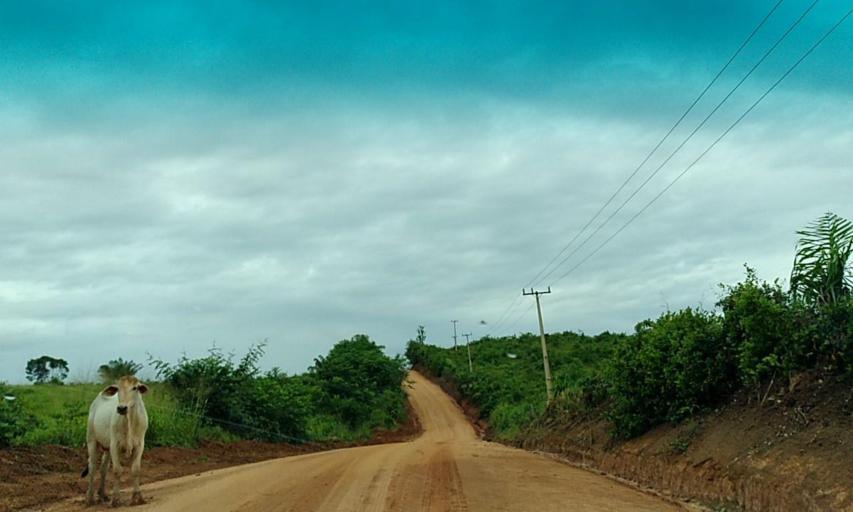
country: BR
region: Para
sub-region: Altamira
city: Altamira
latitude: -3.0837
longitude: -51.6347
